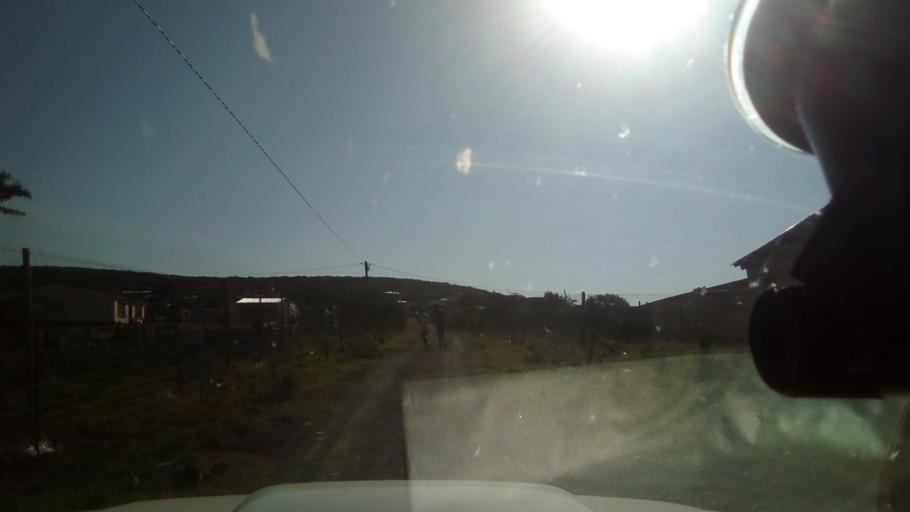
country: ZA
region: Eastern Cape
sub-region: Buffalo City Metropolitan Municipality
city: Bhisho
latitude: -32.8130
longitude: 27.3585
